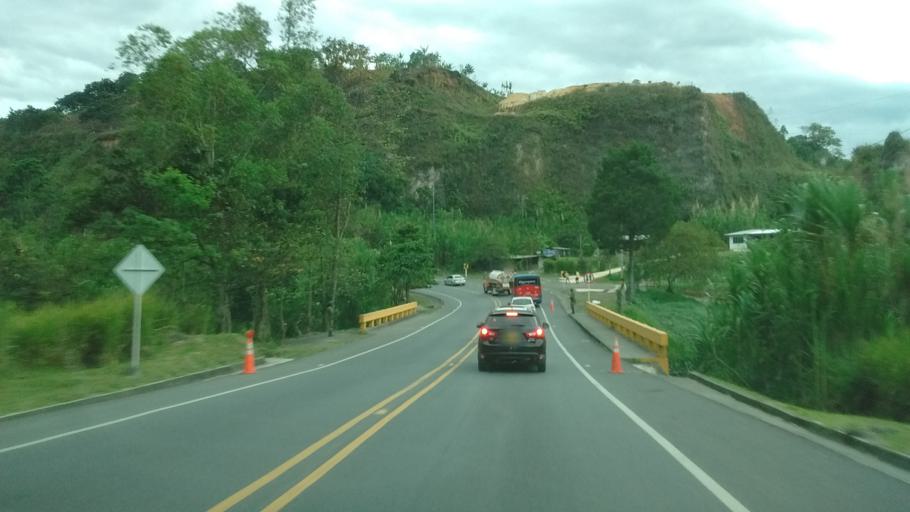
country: CO
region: Cauca
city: Morales
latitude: 2.7256
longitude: -76.5442
